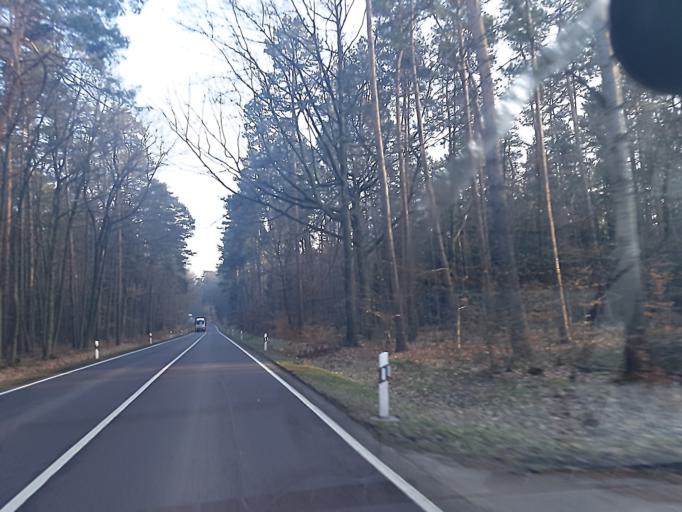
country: DE
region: Brandenburg
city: Wiesenburg
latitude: 52.1322
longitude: 12.4149
